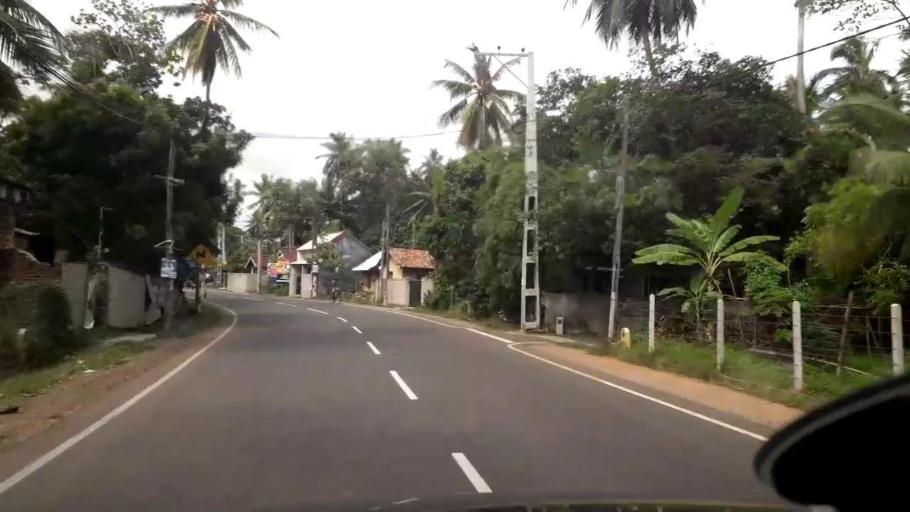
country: LK
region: Western
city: Panadura
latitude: 6.6649
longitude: 79.9331
